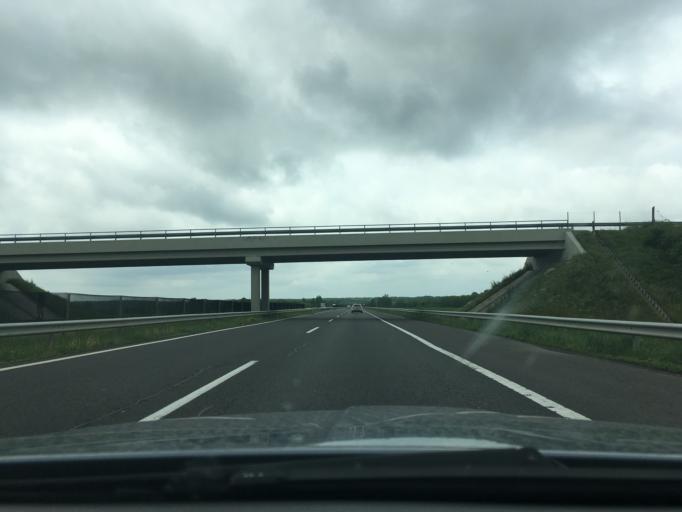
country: HU
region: Hajdu-Bihar
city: Polgar
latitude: 47.8486
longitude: 21.0880
